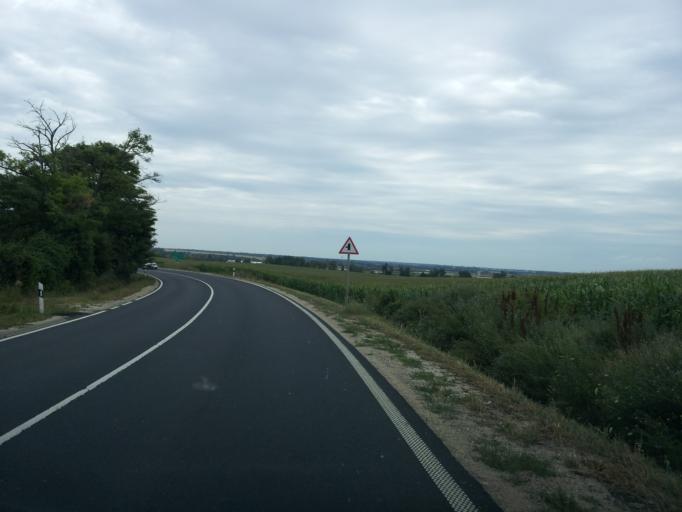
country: HU
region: Fejer
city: Lepseny
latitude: 47.0160
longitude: 18.1784
